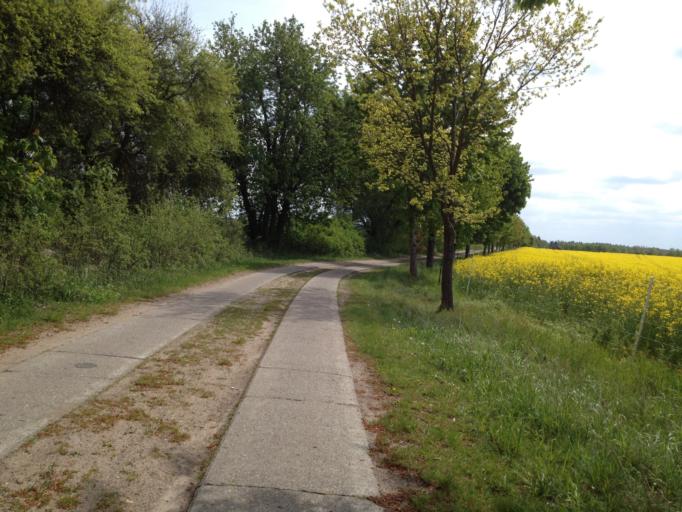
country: DE
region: Brandenburg
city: Lychen
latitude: 53.2774
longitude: 13.3751
